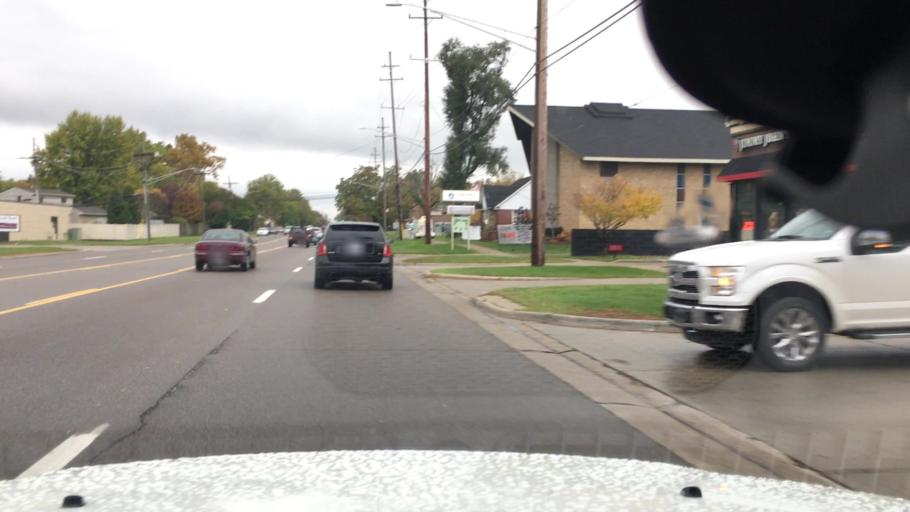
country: US
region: Michigan
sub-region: Oakland County
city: Madison Heights
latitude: 42.5052
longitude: -83.0894
